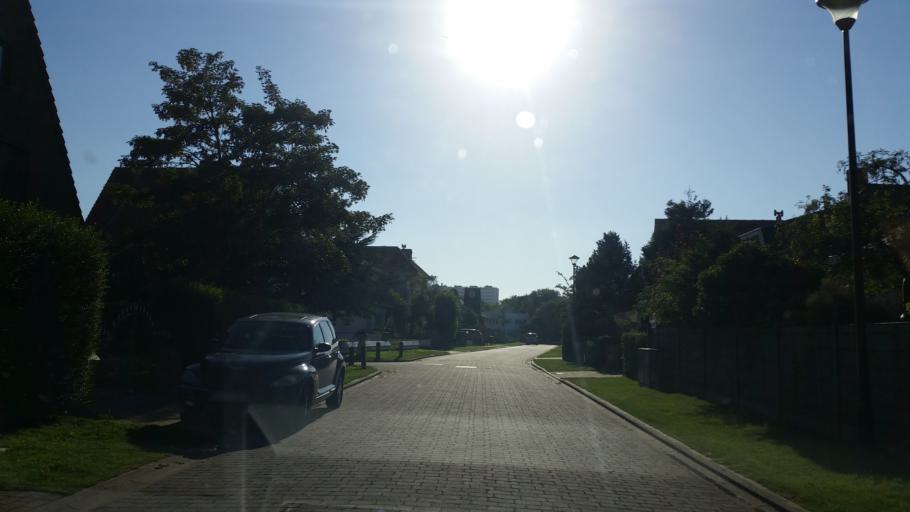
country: BE
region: Flanders
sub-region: Provincie West-Vlaanderen
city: Bredene
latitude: 51.2432
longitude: 2.9571
